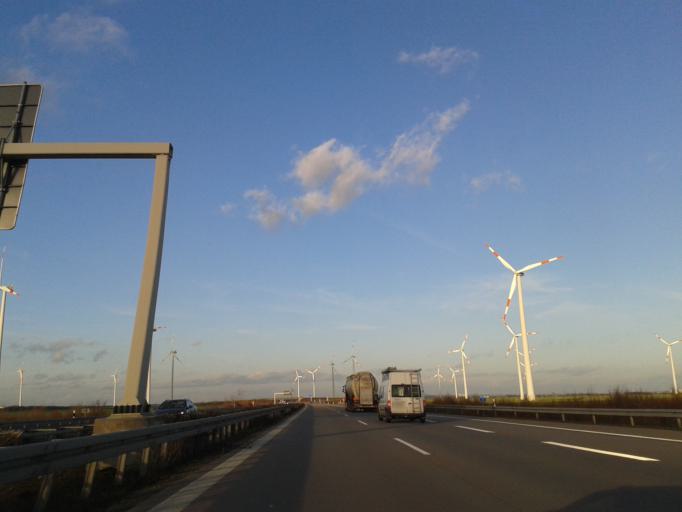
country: DE
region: Saxony-Anhalt
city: Bad Lauchstadt
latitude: 51.4165
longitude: 11.8622
